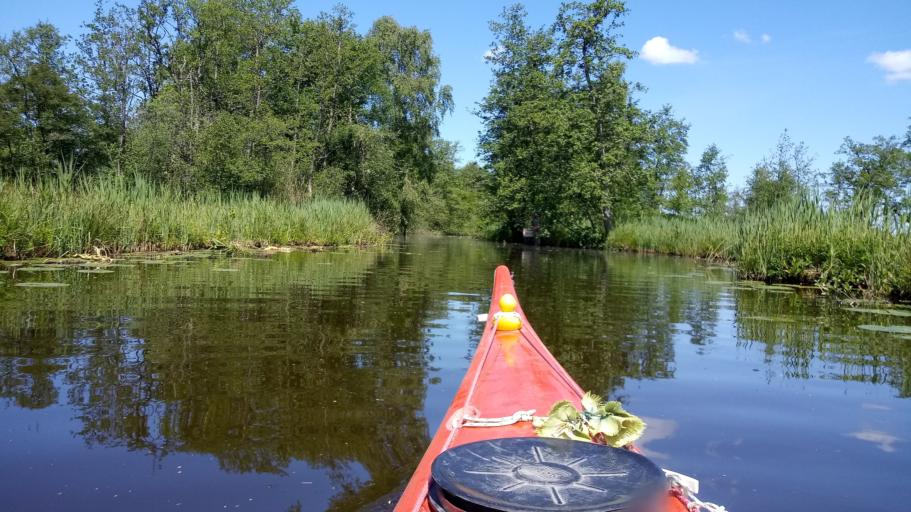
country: NL
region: South Holland
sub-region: Gemeente Nieuwkoop
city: Nieuwkoop
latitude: 52.1578
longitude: 4.8227
